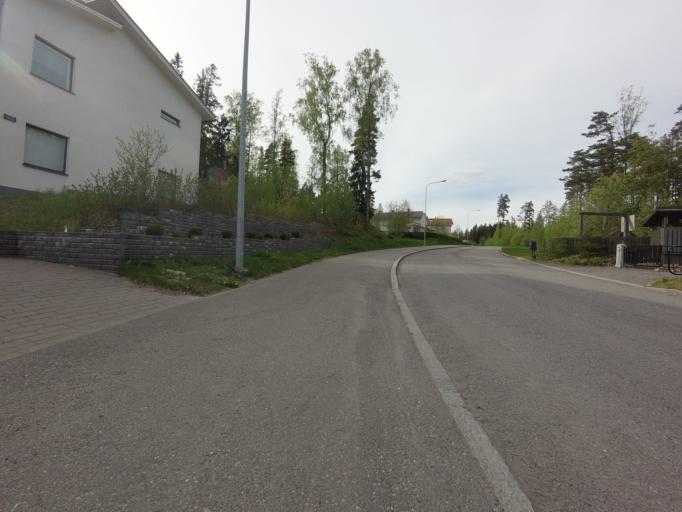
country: FI
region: Uusimaa
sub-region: Helsinki
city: Kauniainen
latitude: 60.1950
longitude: 24.7202
